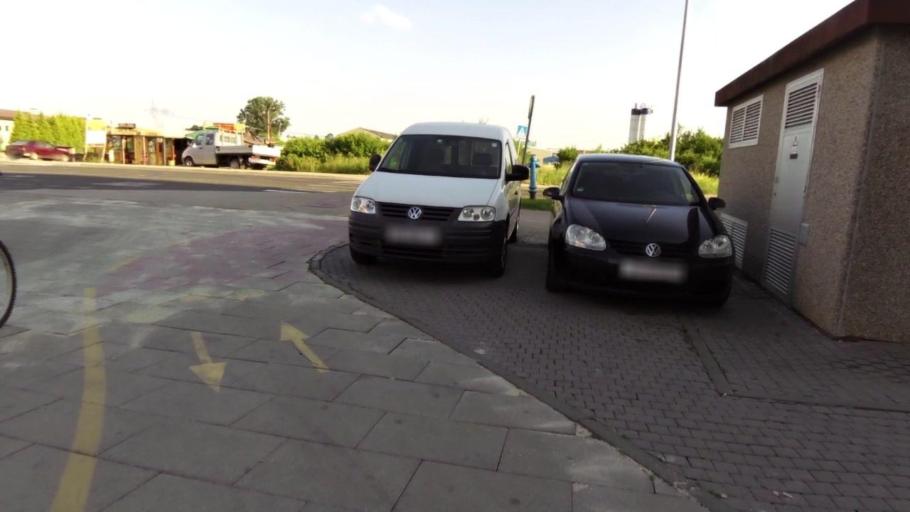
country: HR
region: Grad Zagreb
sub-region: Sesvete
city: Sesvete
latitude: 45.8100
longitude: 16.1032
